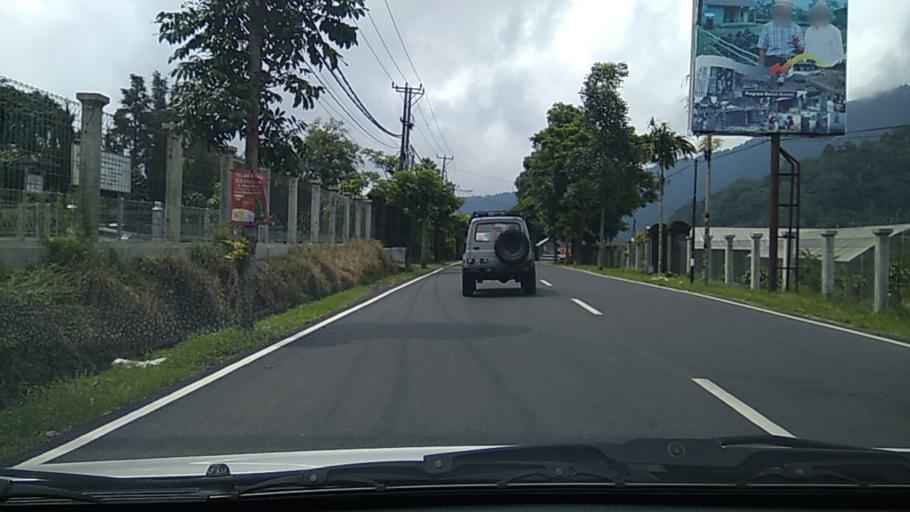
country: ID
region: Bali
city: Munduk
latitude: -8.2616
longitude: 115.1638
